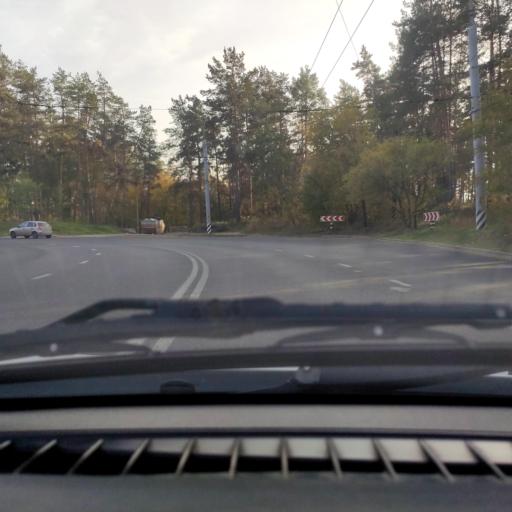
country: RU
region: Samara
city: Zhigulevsk
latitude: 53.4883
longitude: 49.4626
